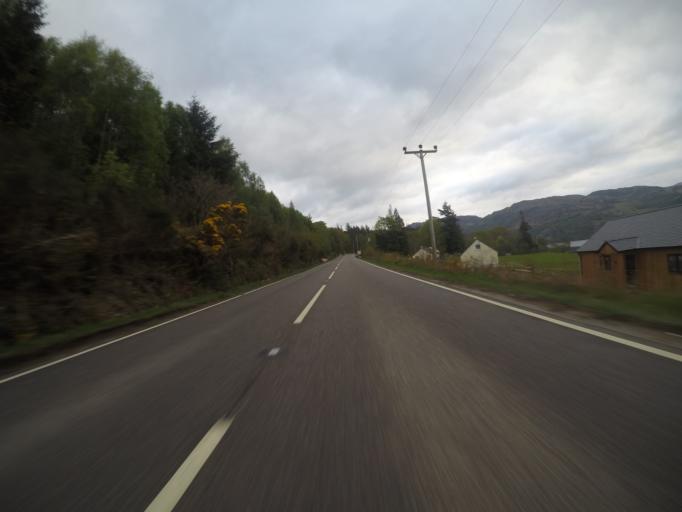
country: GB
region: Scotland
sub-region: Highland
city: Spean Bridge
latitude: 57.1581
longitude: -4.6657
